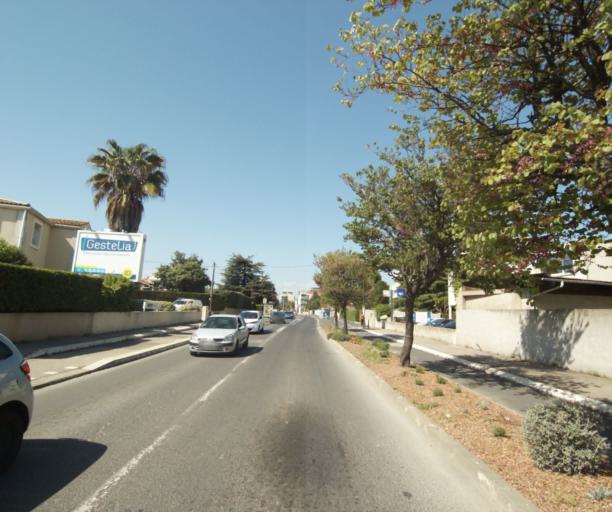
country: FR
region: Languedoc-Roussillon
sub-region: Departement de l'Herault
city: Castelnau-le-Lez
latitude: 43.6131
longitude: 3.8982
